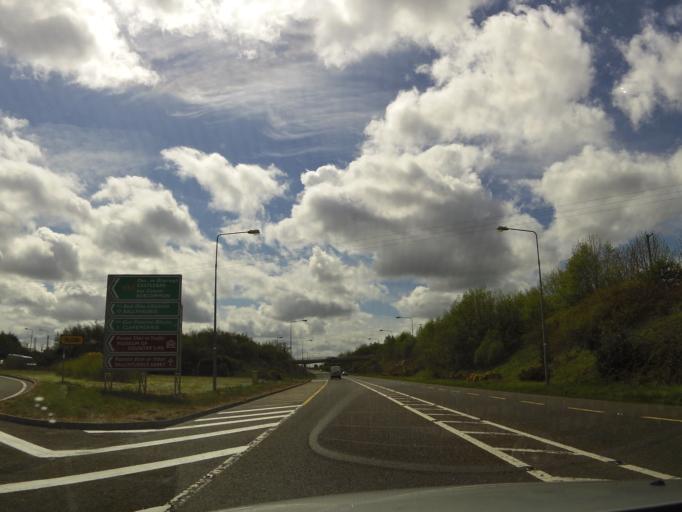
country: IE
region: Connaught
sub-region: Maigh Eo
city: Claremorris
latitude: 53.7261
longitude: -8.9822
